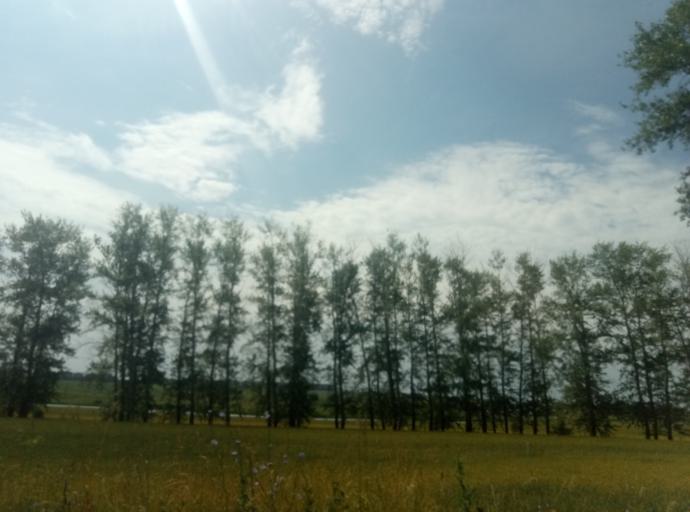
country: RU
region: Tula
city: Kireyevsk
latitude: 53.8976
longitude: 37.9898
